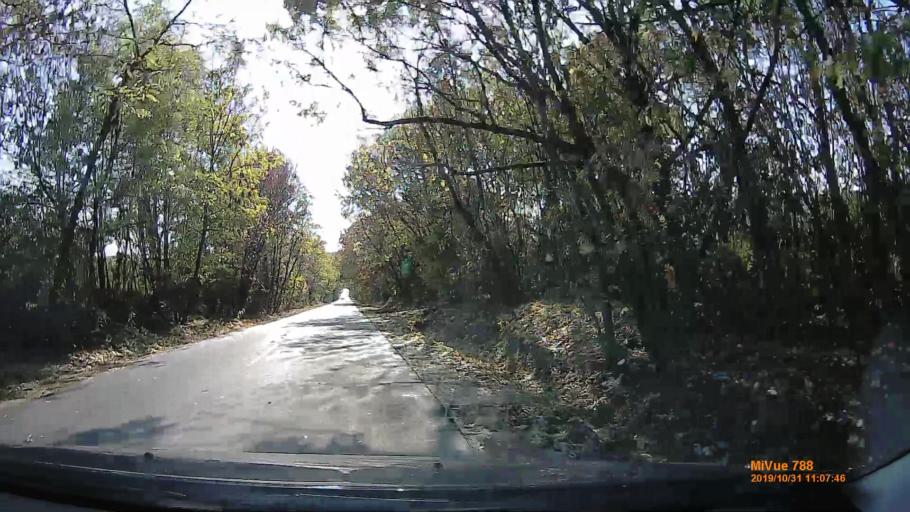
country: HU
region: Pest
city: Urom
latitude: 47.5940
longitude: 19.0016
